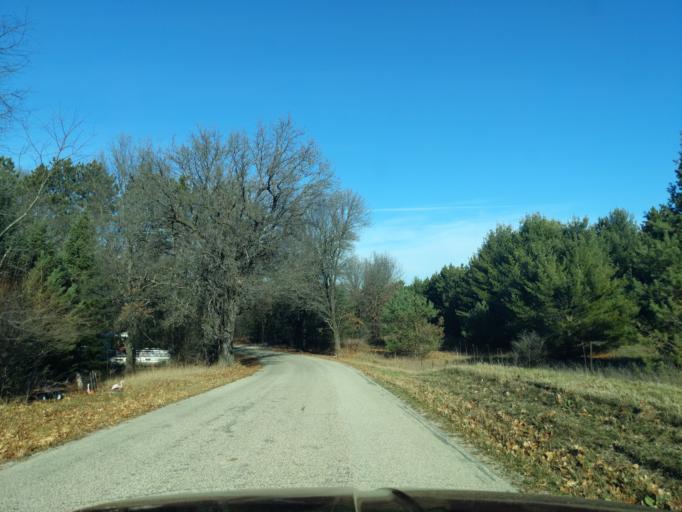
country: US
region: Wisconsin
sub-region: Waushara County
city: Silver Lake
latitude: 44.1093
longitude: -89.1689
